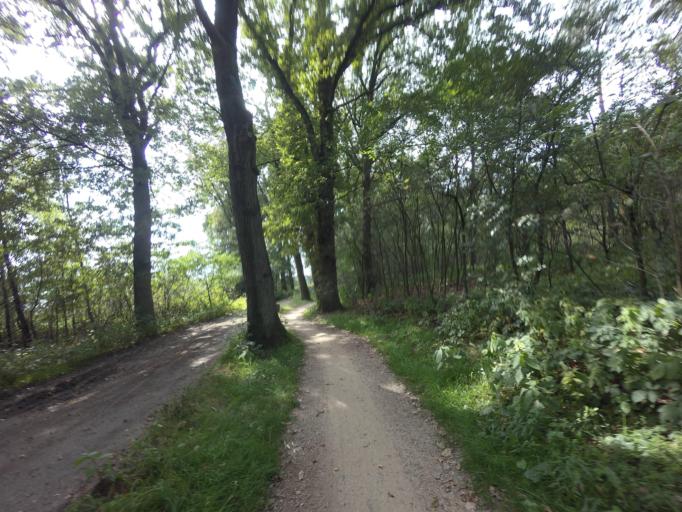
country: NL
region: Overijssel
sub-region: Gemeente Losser
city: Losser
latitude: 52.3242
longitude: 7.0357
